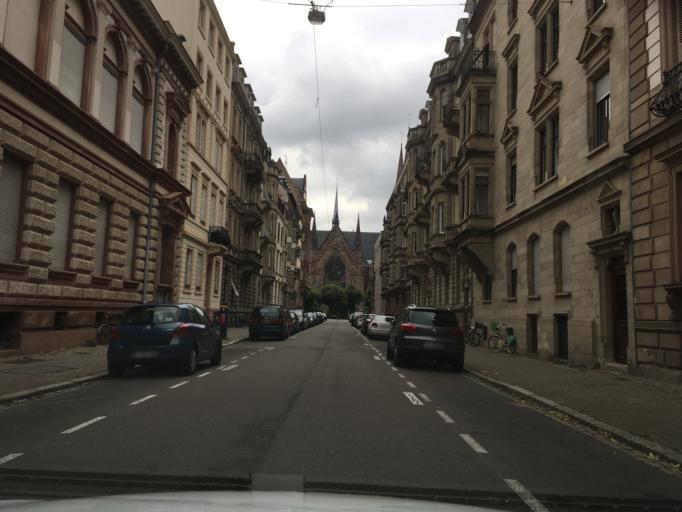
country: FR
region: Alsace
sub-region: Departement du Bas-Rhin
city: Strasbourg
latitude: 48.5872
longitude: 7.7570
